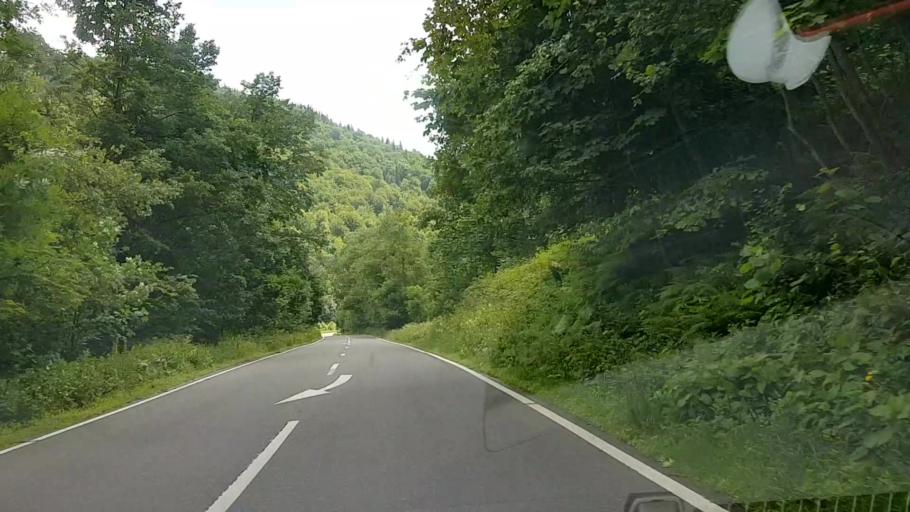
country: RO
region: Suceava
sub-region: Comuna Crucea
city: Crucea
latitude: 47.3238
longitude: 25.6240
